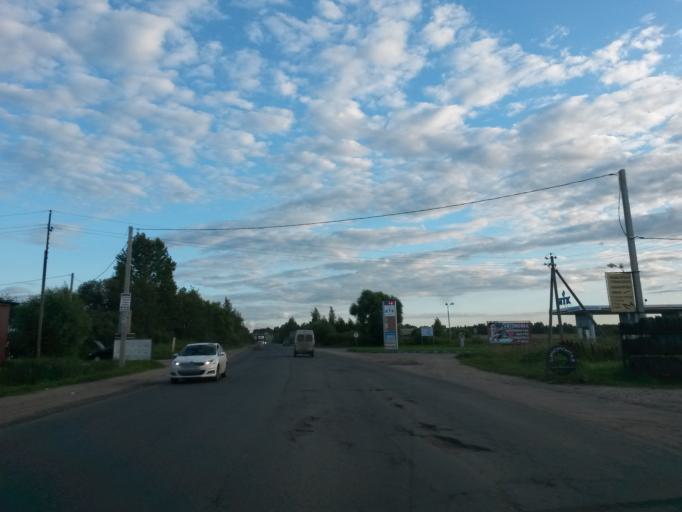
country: RU
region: Jaroslavl
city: Yaroslavl
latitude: 57.5668
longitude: 39.8587
